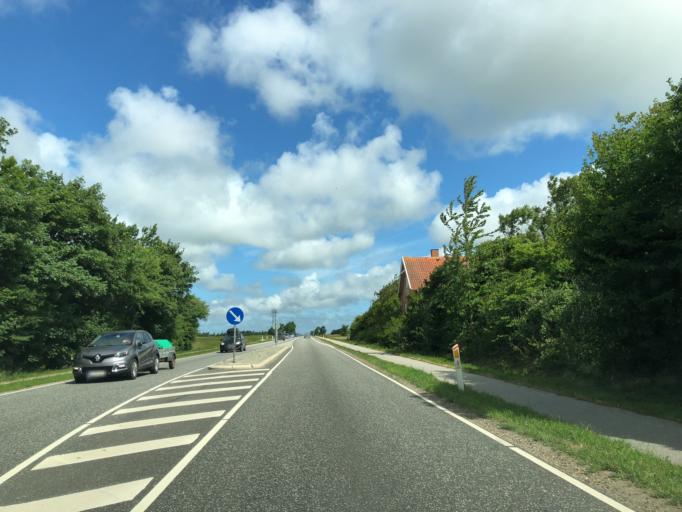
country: DK
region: Central Jutland
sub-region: Holstebro Kommune
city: Holstebro
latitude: 56.3958
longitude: 8.6089
